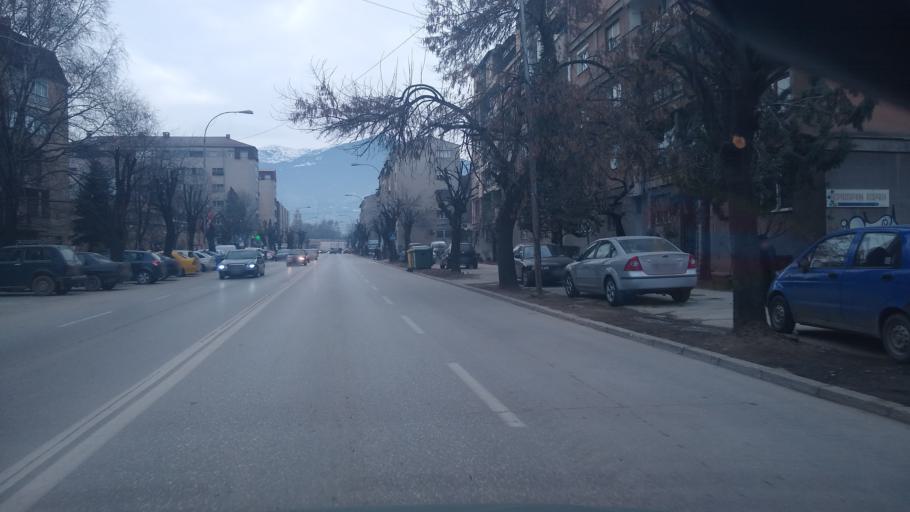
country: MK
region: Bitola
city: Bitola
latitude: 41.0345
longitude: 21.3390
